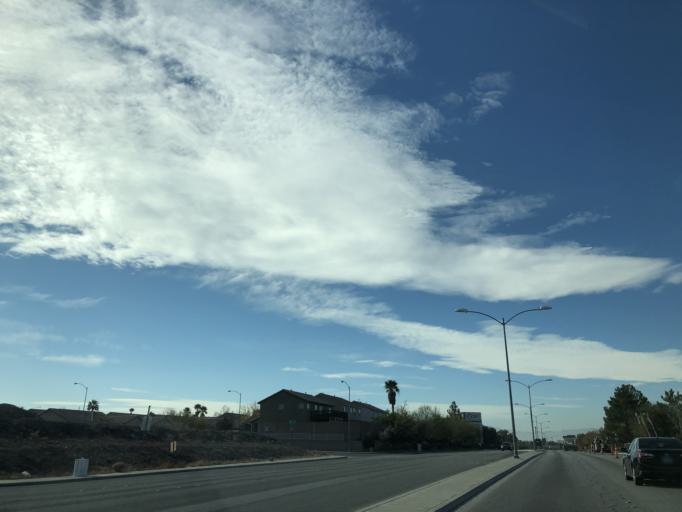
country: US
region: Nevada
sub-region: Clark County
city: Henderson
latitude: 36.0220
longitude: -115.0409
